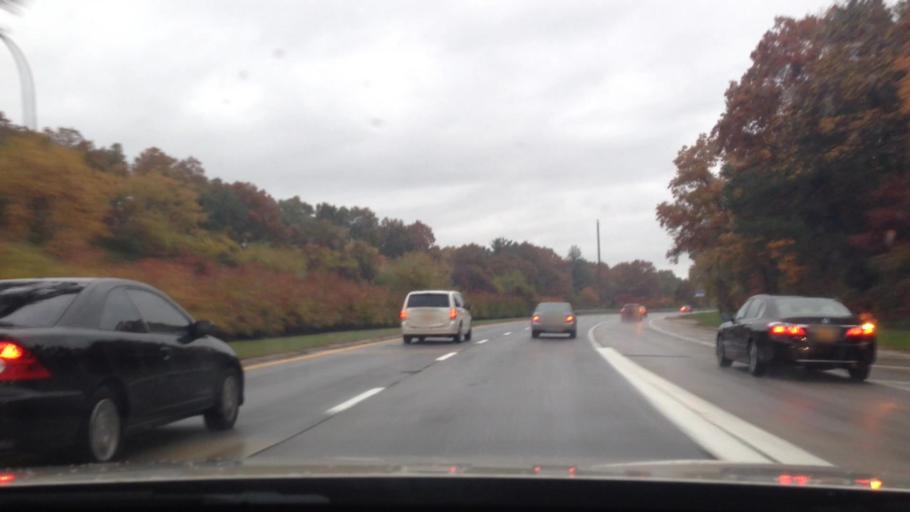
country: US
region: New York
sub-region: Suffolk County
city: Bay Wood
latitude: 40.7483
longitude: -73.2794
